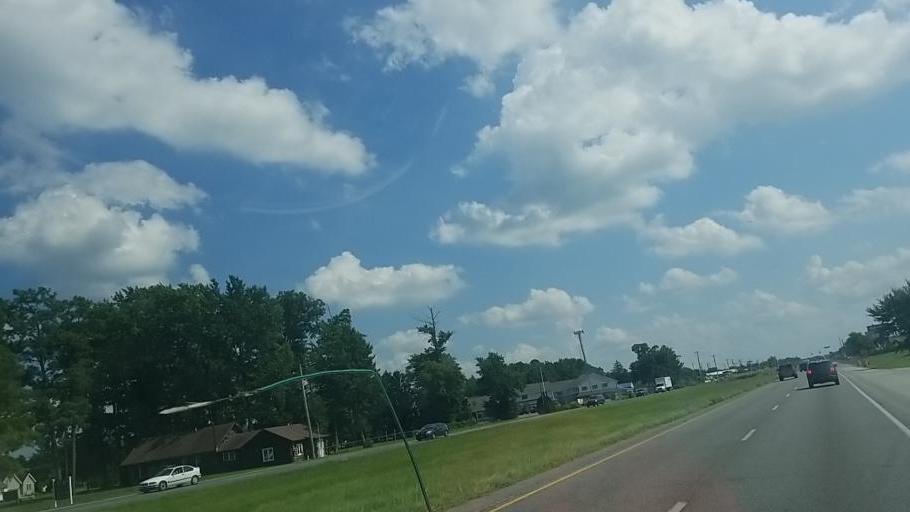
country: US
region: Delaware
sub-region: Sussex County
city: Georgetown
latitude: 38.7051
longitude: -75.4029
